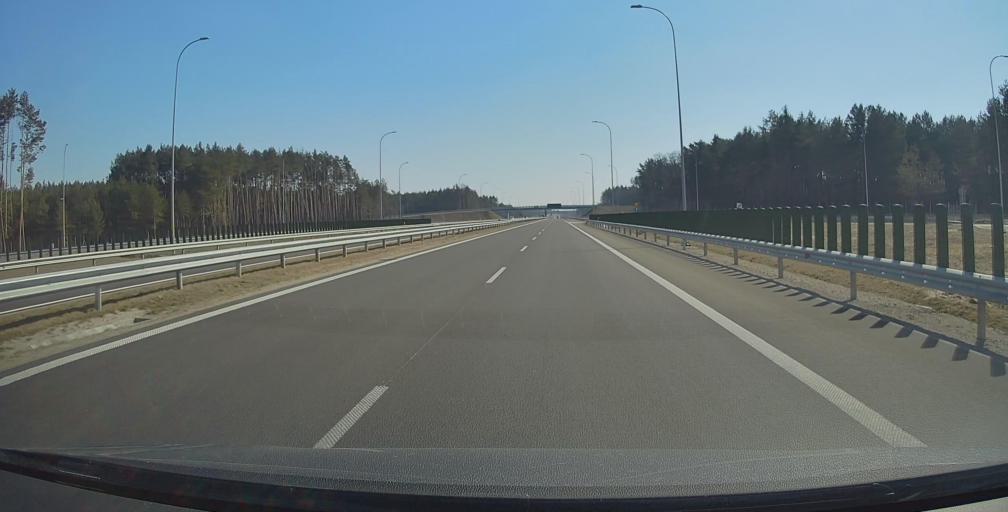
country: PL
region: Subcarpathian Voivodeship
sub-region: Powiat nizanski
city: Jezowe
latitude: 50.3865
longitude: 22.1595
